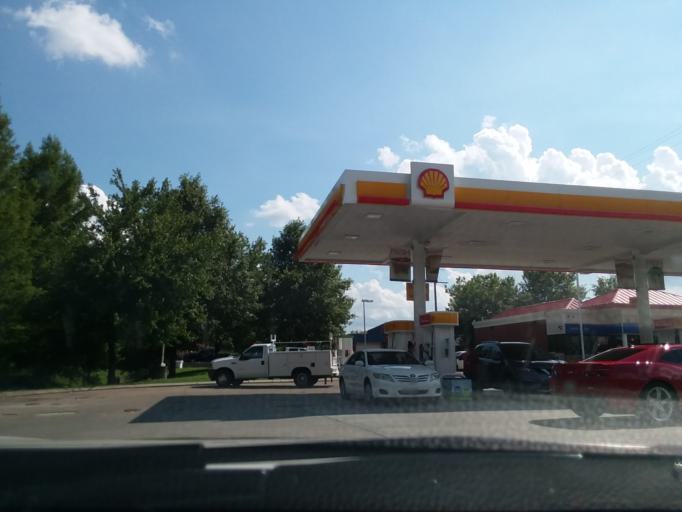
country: US
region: Tennessee
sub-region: Davidson County
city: Goodlettsville
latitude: 36.2690
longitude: -86.7549
